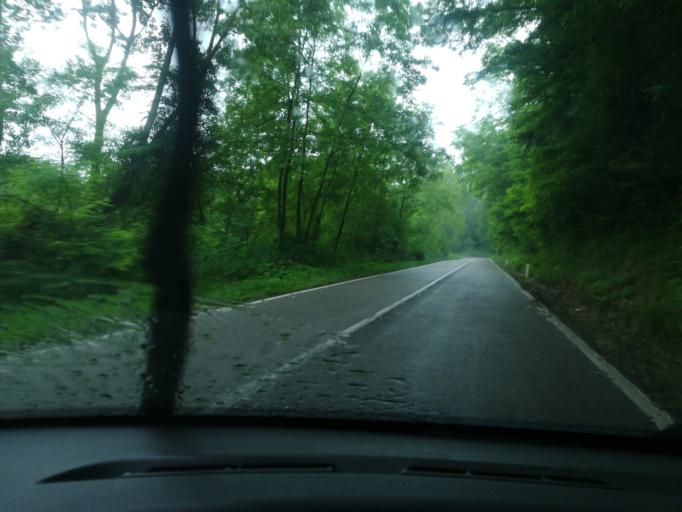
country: IT
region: The Marches
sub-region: Provincia di Macerata
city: Sarnano
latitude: 43.0168
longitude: 13.3236
